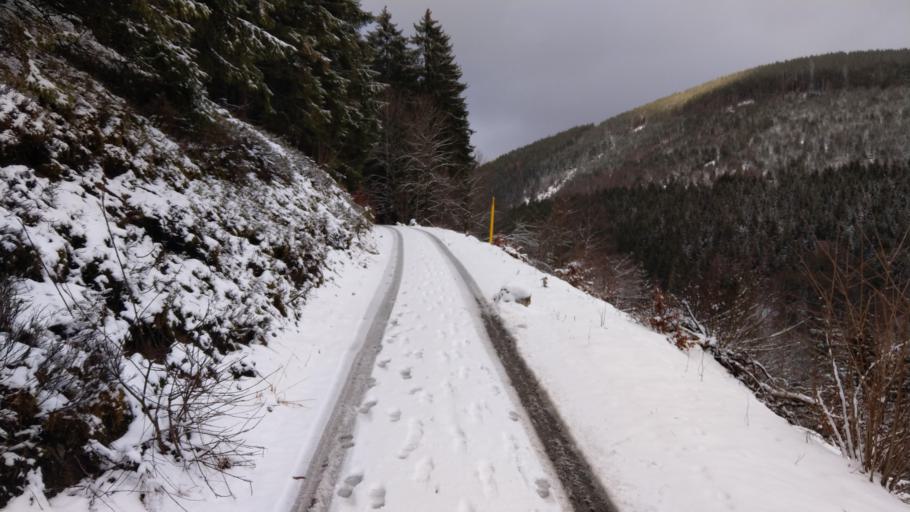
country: DE
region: Hesse
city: Willingen
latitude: 51.2988
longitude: 8.5933
